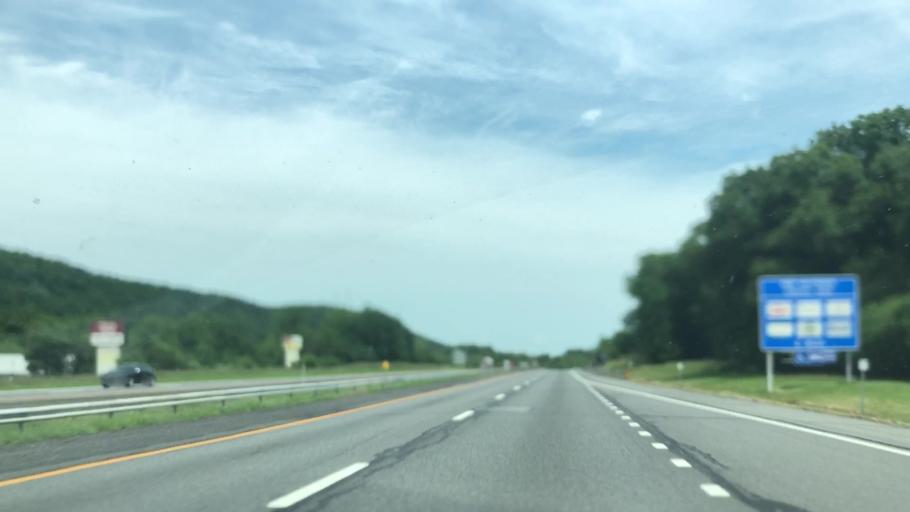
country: US
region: New York
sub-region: Greene County
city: Coxsackie
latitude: 42.3963
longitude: -73.8241
